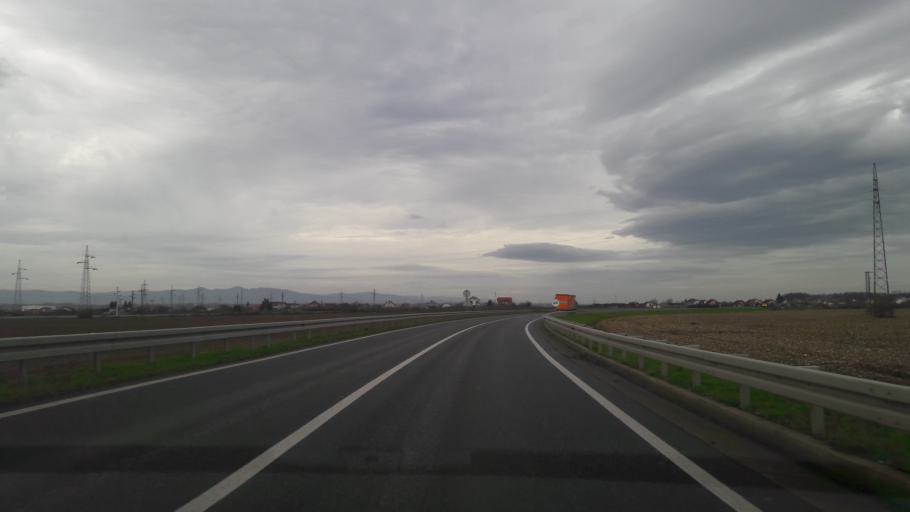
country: HR
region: Osjecko-Baranjska
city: Velimirovac
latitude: 45.5107
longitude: 18.1047
